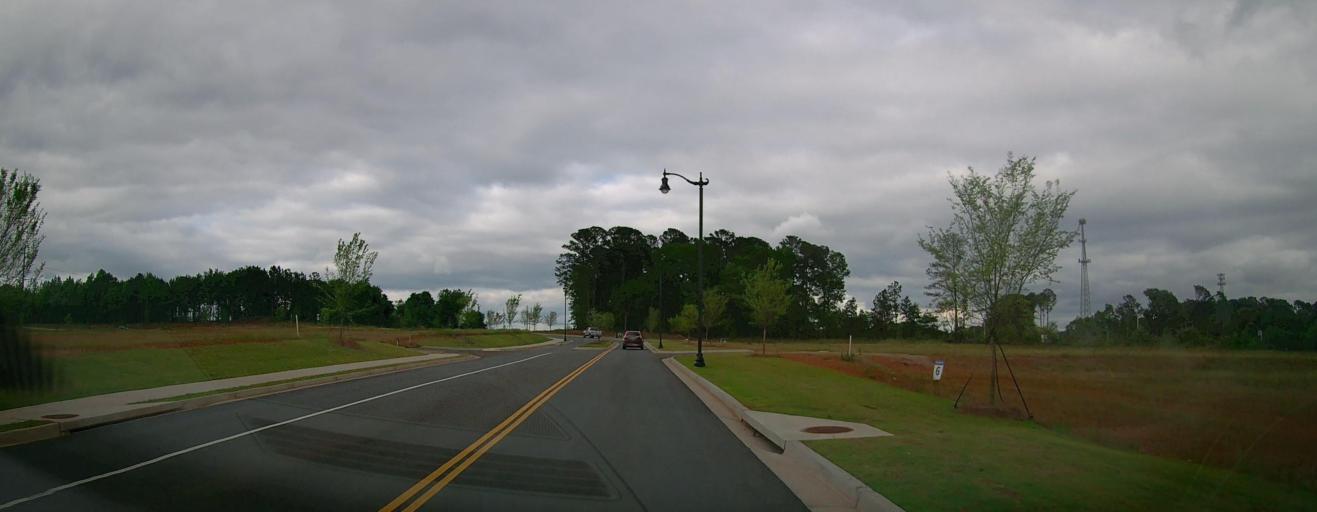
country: US
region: Georgia
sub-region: Walton County
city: Monroe
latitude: 33.8058
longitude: -83.7275
